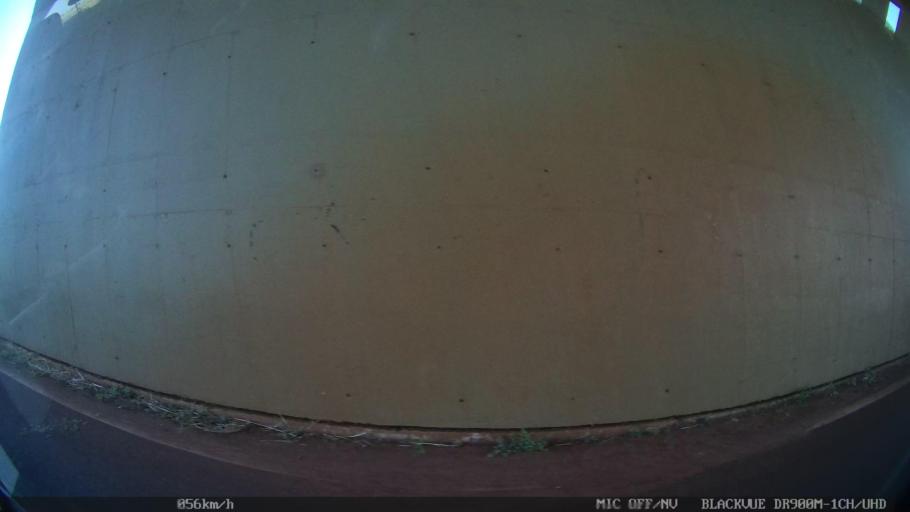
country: BR
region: Sao Paulo
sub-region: Barretos
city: Barretos
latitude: -20.5270
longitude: -48.5903
